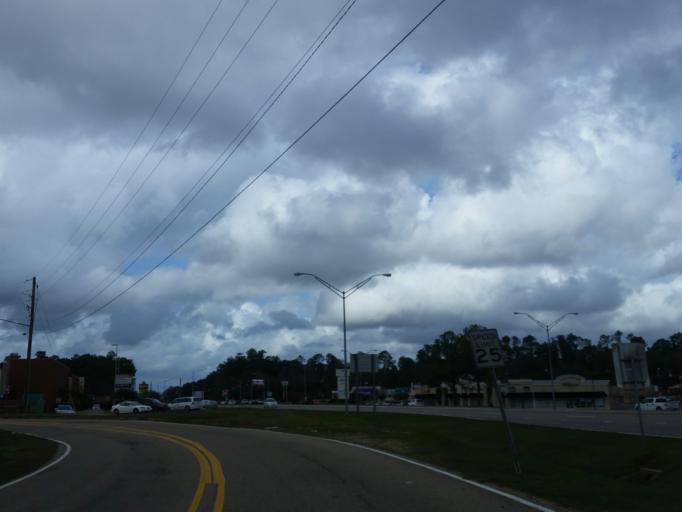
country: US
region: Mississippi
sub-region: Forrest County
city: Hattiesburg
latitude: 31.3090
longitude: -89.3187
